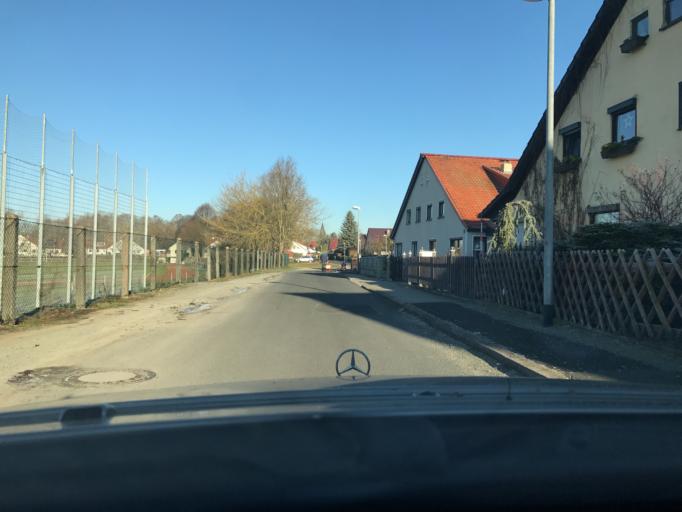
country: DE
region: Thuringia
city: Muehlhausen
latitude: 51.2308
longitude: 10.4489
